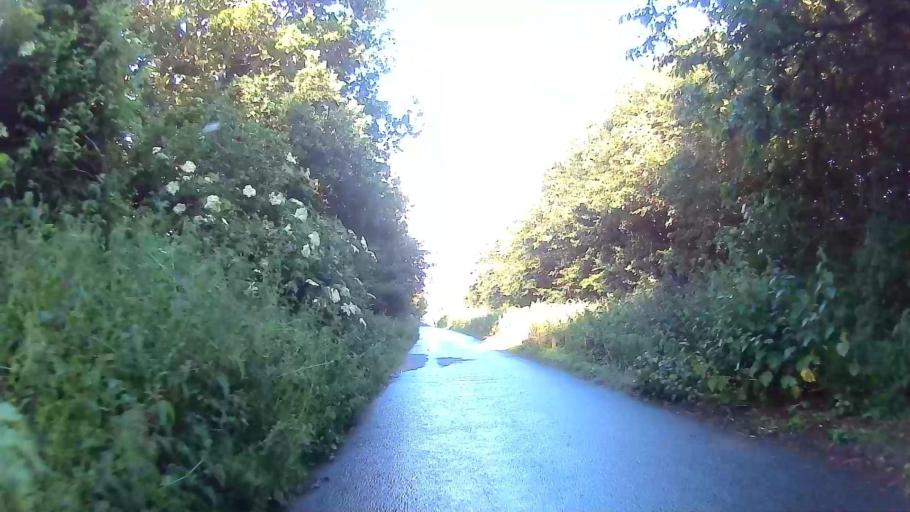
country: GB
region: England
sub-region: Essex
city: Writtle
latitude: 51.7360
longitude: 0.4329
